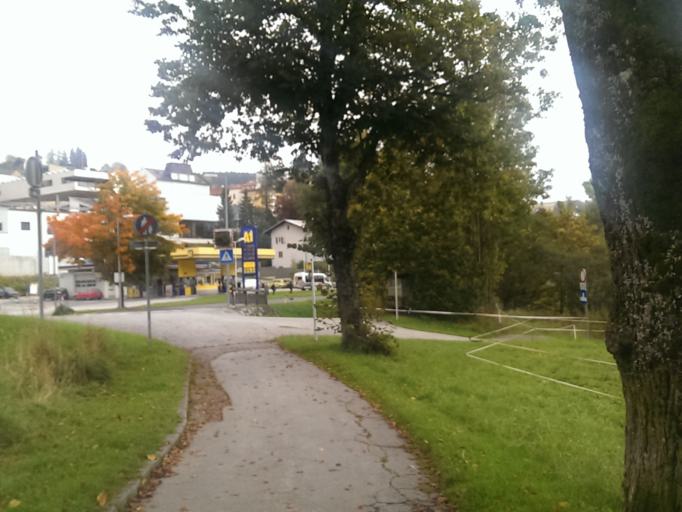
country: AT
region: Styria
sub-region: Politischer Bezirk Bruck-Muerzzuschlag
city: Mariazell
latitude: 47.7745
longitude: 15.3143
